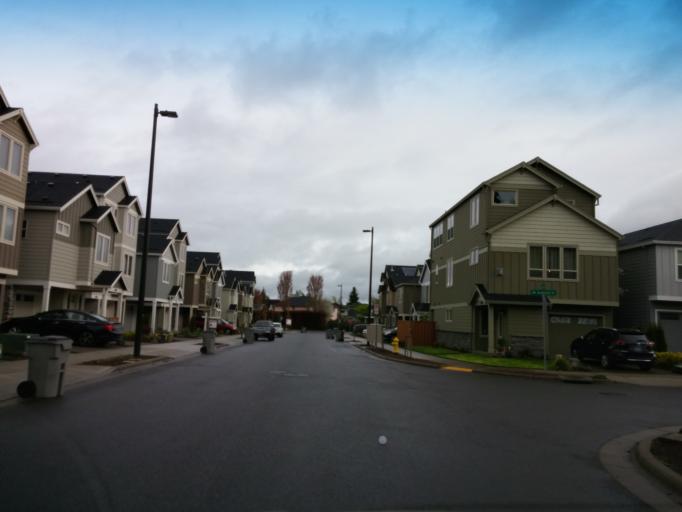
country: US
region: Oregon
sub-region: Washington County
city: Oak Hills
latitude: 45.5350
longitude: -122.8453
